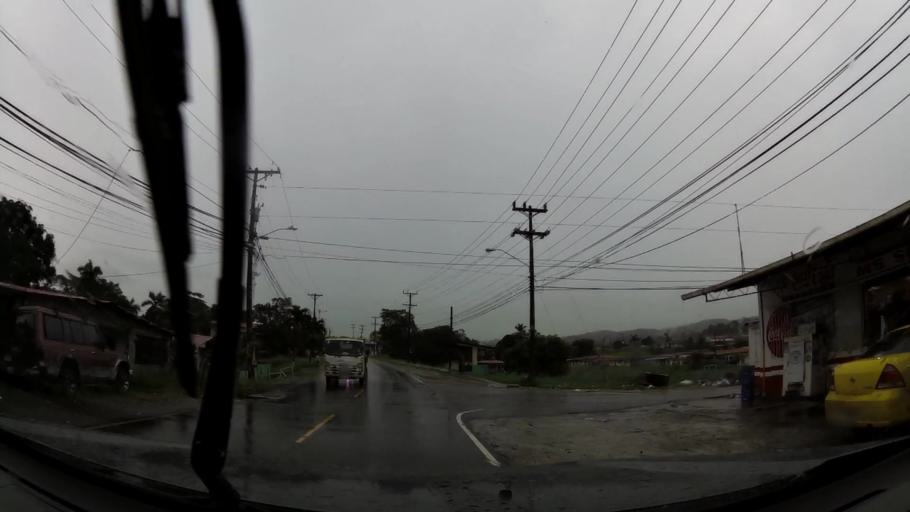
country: PA
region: Colon
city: Puerto Pilon
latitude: 9.3574
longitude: -79.7958
